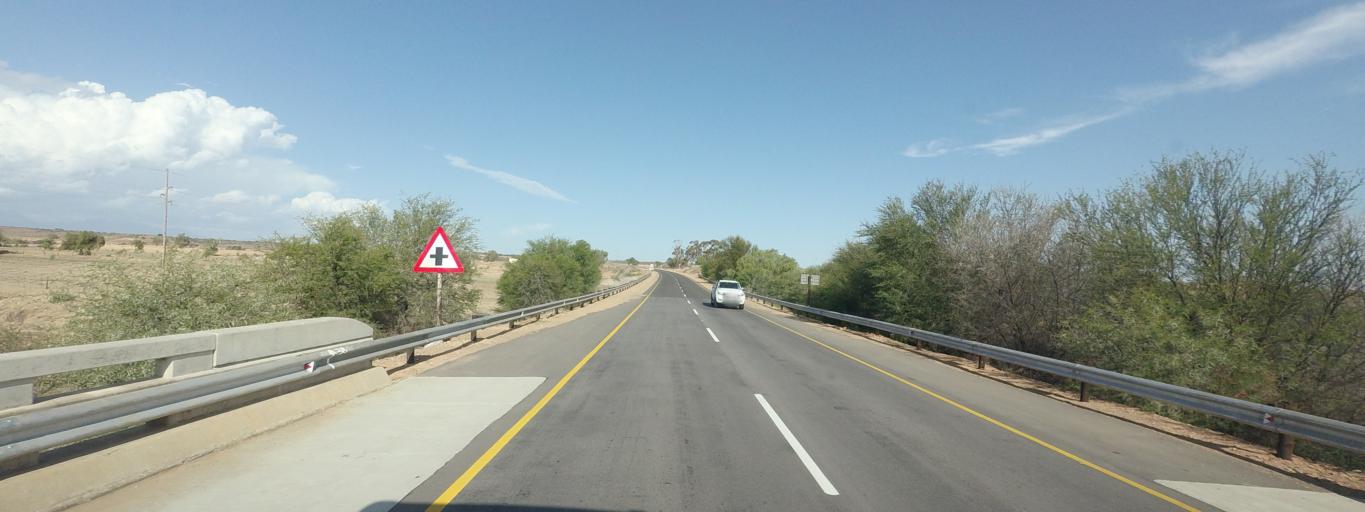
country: ZA
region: Western Cape
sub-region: Eden District Municipality
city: Oudtshoorn
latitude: -33.6029
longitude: 22.0605
